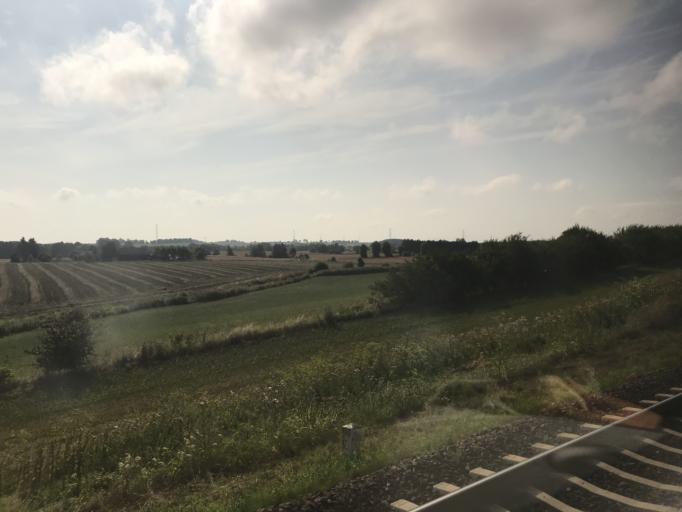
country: PL
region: Pomeranian Voivodeship
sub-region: Powiat starogardzki
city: Smetowo Graniczne
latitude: 53.7387
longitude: 18.6856
